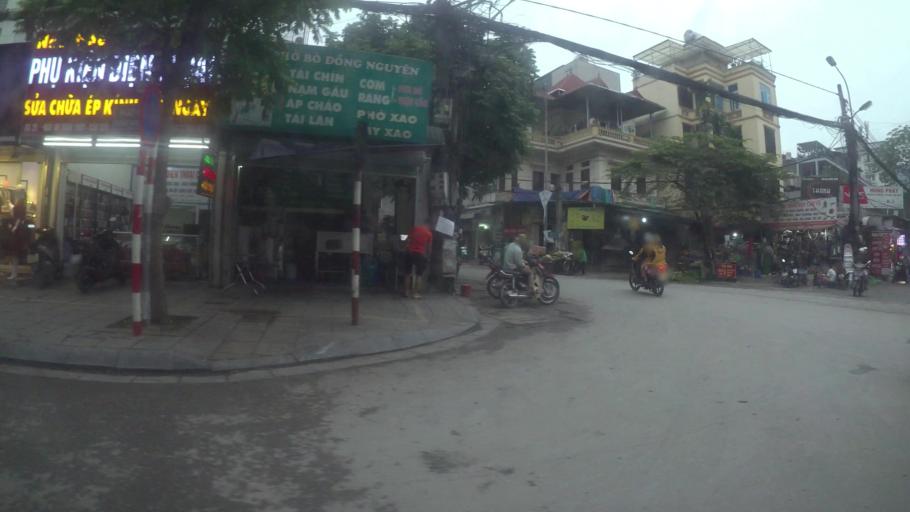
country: VN
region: Ha Noi
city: Cau Giay
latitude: 21.0344
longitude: 105.7835
